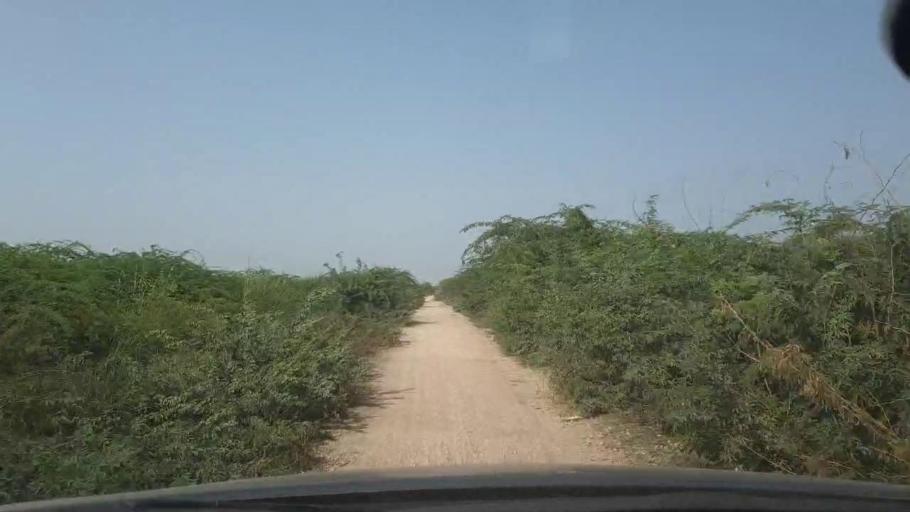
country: PK
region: Sindh
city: Naukot
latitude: 24.7969
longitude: 69.2410
